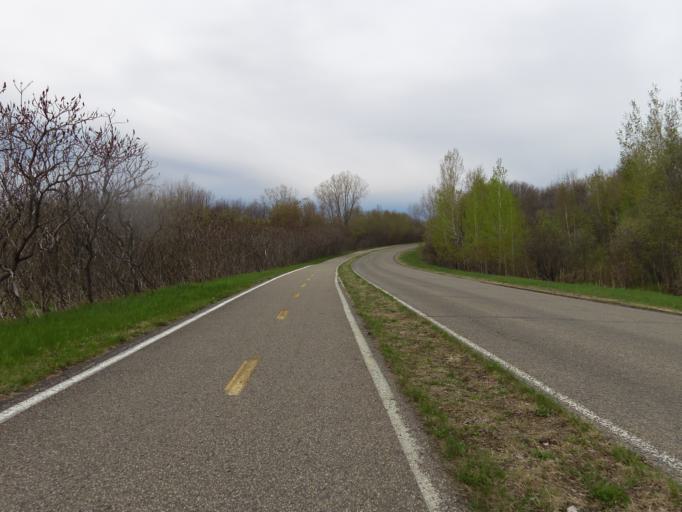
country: CA
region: Quebec
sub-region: Laurentides
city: Oka
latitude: 45.4797
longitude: -74.0442
